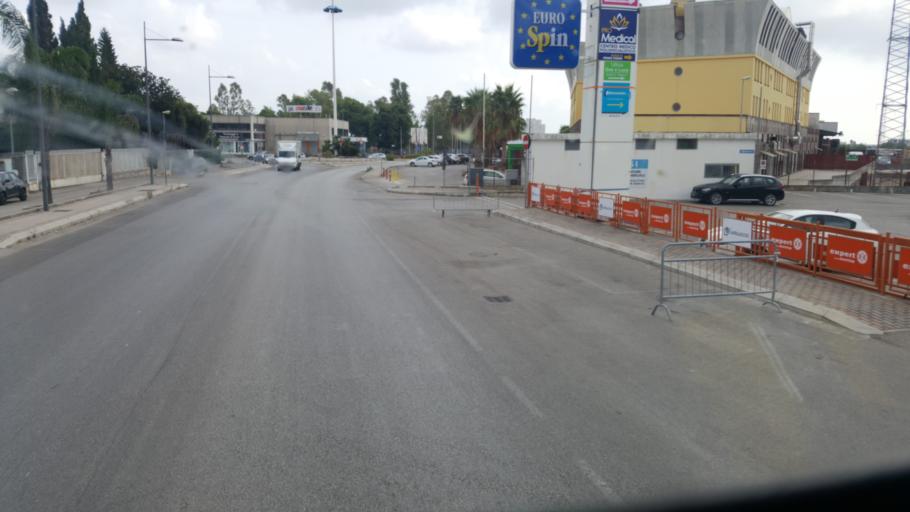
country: IT
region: Campania
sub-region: Provincia di Salerno
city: Battipaglia
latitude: 40.5970
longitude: 14.9885
